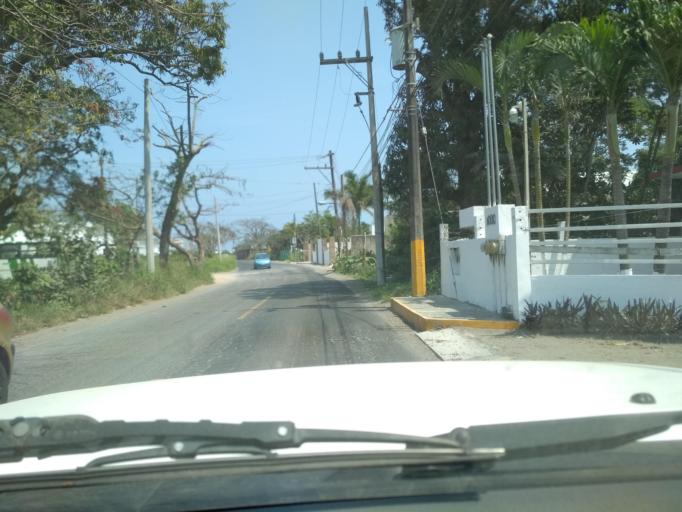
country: MX
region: Veracruz
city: Boca del Rio
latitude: 19.0958
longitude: -96.1249
